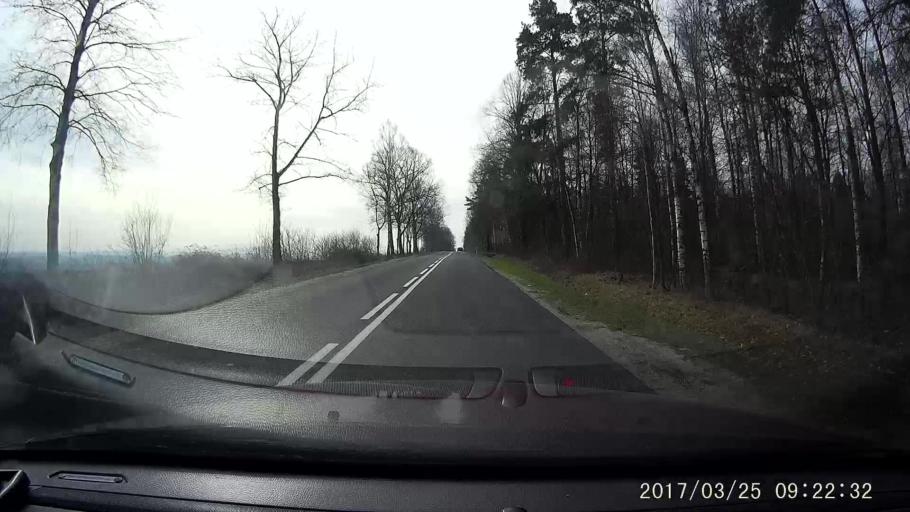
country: PL
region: Lower Silesian Voivodeship
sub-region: Powiat zgorzelecki
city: Sulikow
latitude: 51.0741
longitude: 15.0293
